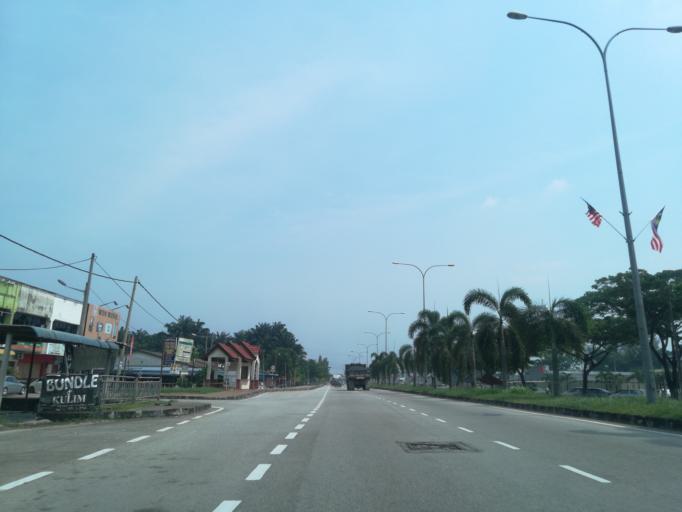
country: MY
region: Kedah
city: Kulim
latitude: 5.4034
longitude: 100.5542
